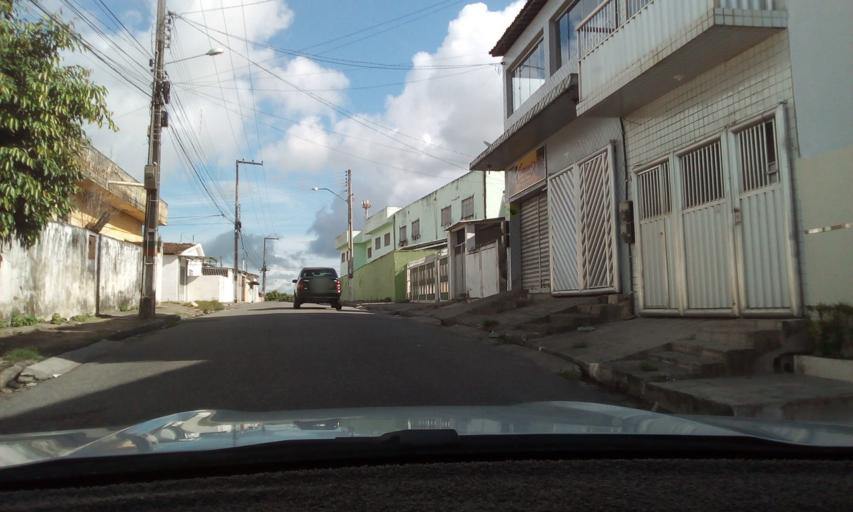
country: BR
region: Paraiba
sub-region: Bayeux
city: Bayeux
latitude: -7.1305
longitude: -34.9215
